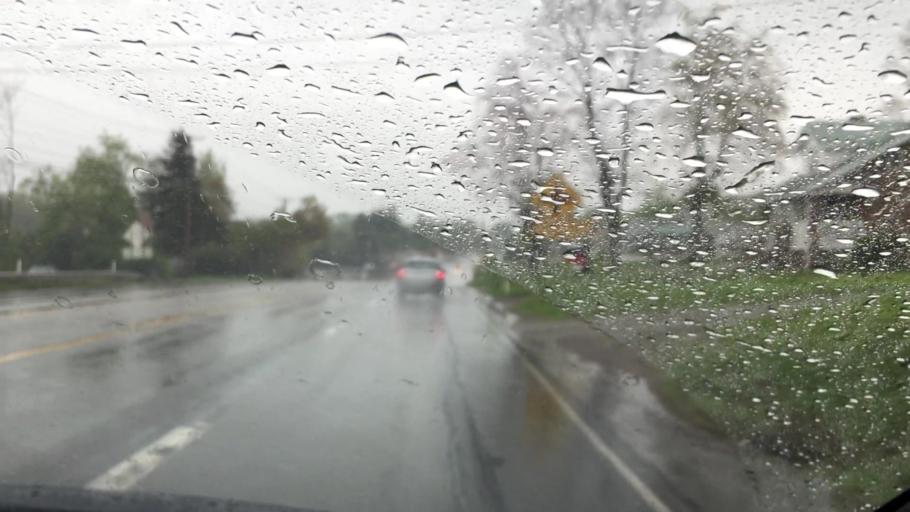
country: US
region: Pennsylvania
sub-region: Butler County
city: Nixon
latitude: 40.7425
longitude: -79.9251
